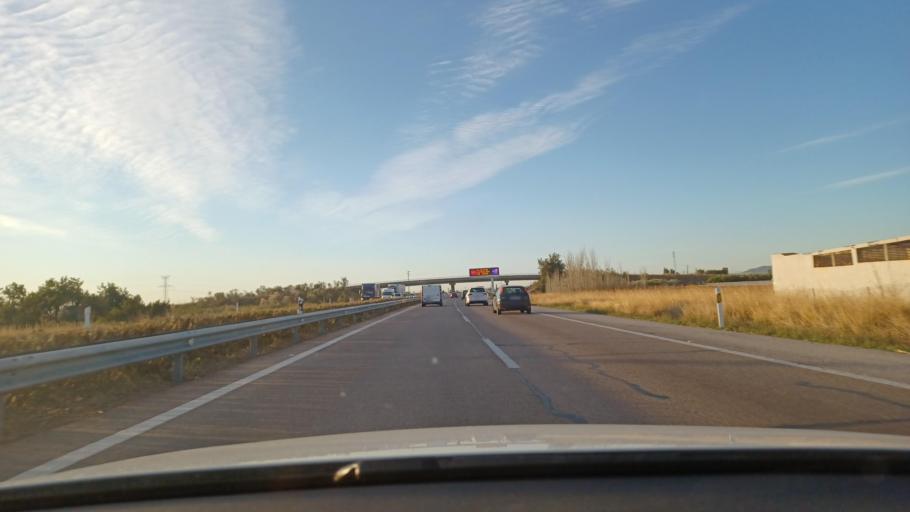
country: ES
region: Valencia
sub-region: Provincia de Castello
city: Vila-real
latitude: 39.9537
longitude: -0.1293
